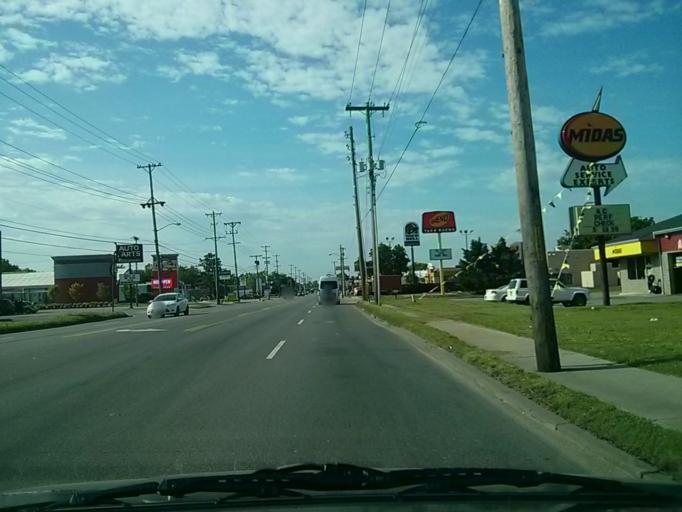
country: US
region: Oklahoma
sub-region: Tulsa County
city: Tulsa
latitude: 36.0972
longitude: -95.9758
